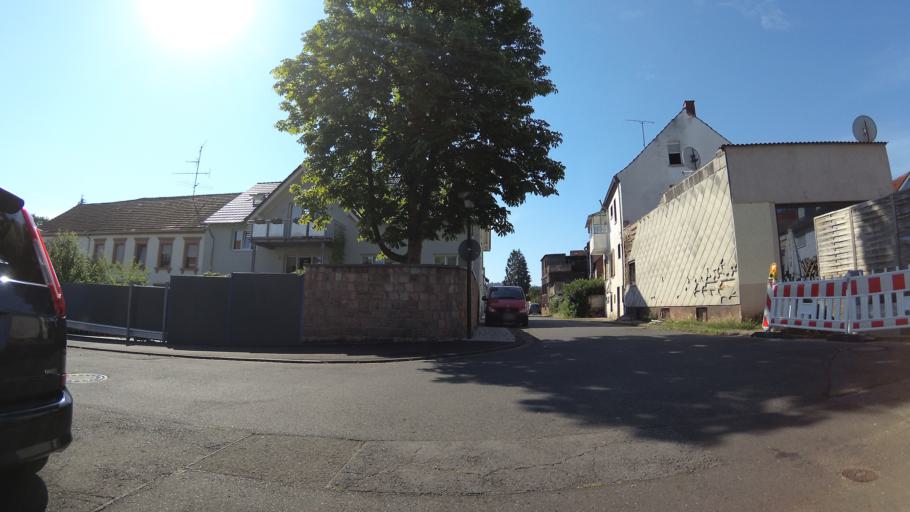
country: DE
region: Saarland
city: Homburg
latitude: 49.3355
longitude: 7.3356
